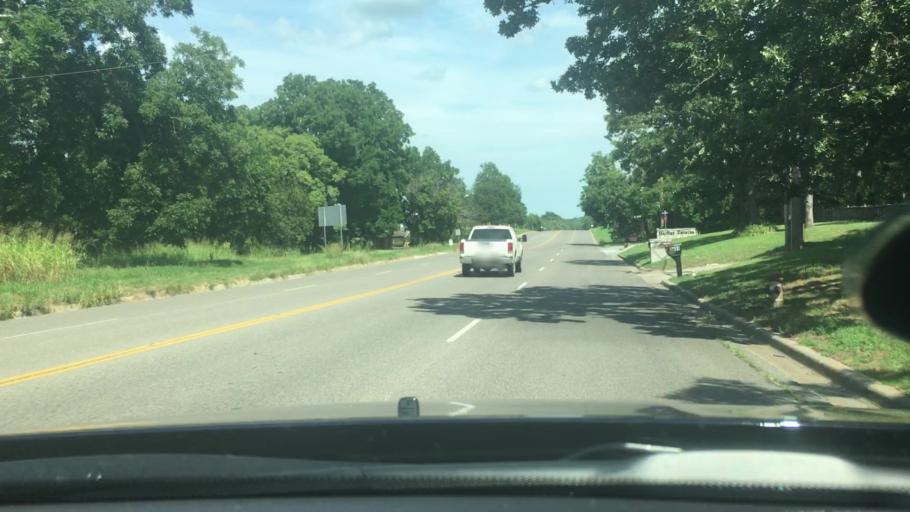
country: US
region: Oklahoma
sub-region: Pottawatomie County
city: Shawnee
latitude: 35.3326
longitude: -96.8915
